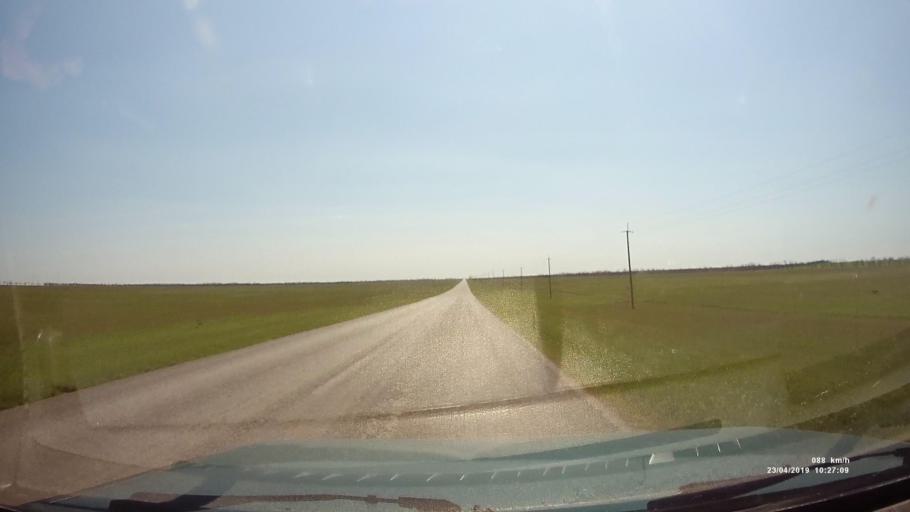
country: RU
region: Kalmykiya
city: Yashalta
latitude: 46.6160
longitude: 42.4866
